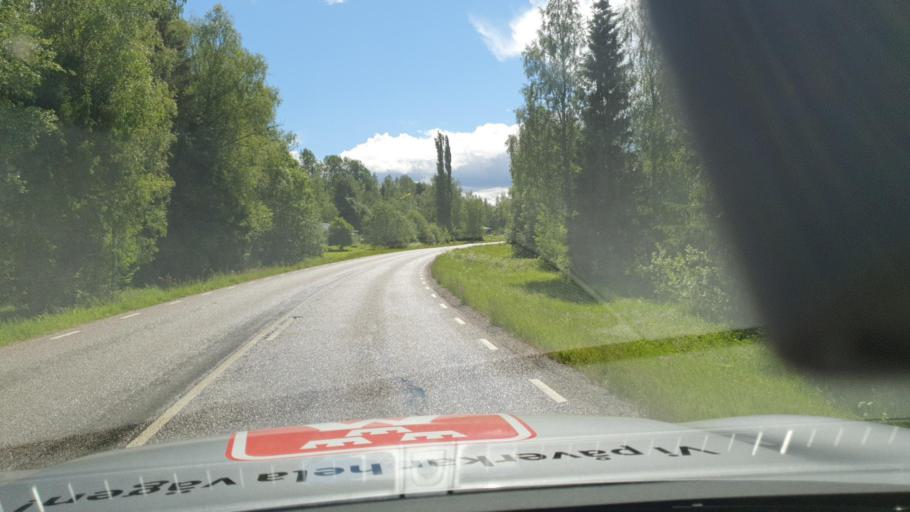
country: SE
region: Vaesternorrland
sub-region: OErnskoeldsviks Kommun
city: Bjasta
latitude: 63.2829
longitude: 18.2970
